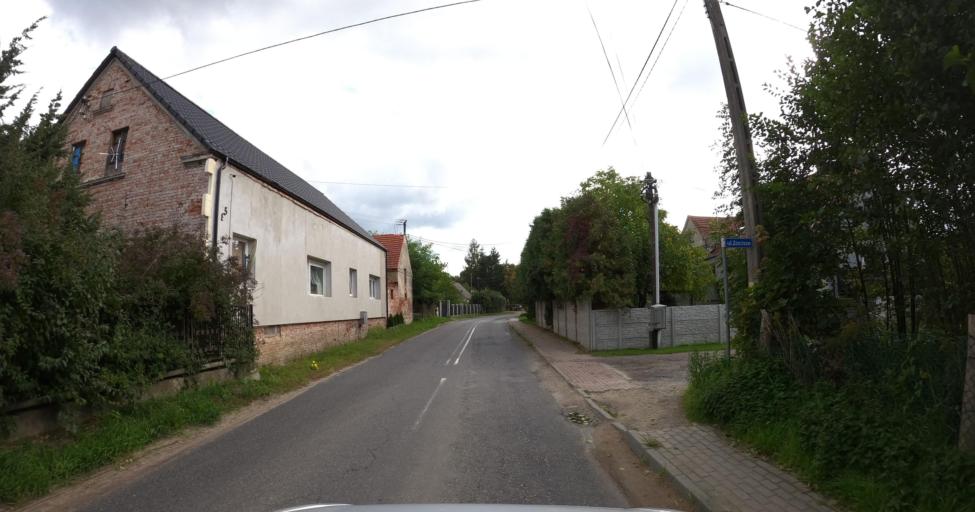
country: PL
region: Lubusz
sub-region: Powiat zielonogorski
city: Zabor
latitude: 51.9549
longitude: 15.6307
